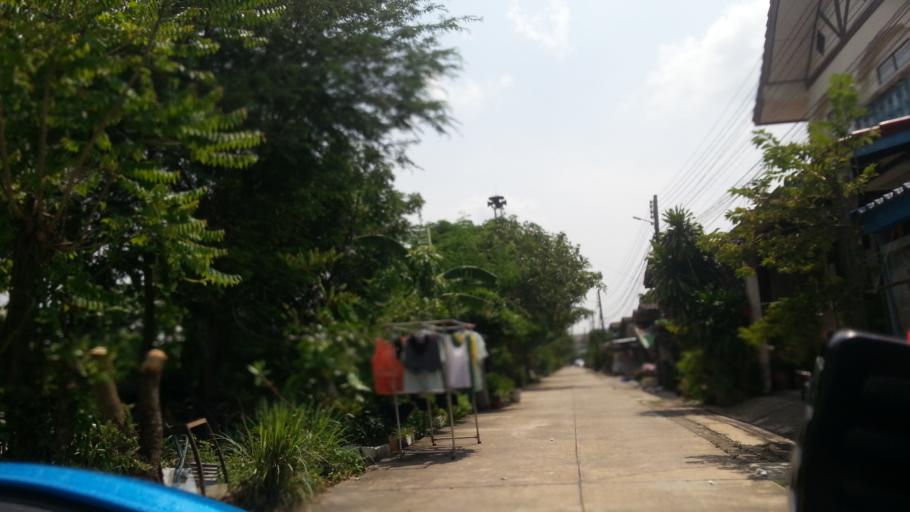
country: TH
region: Pathum Thani
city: Ban Rangsit
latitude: 14.0570
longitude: 100.8266
